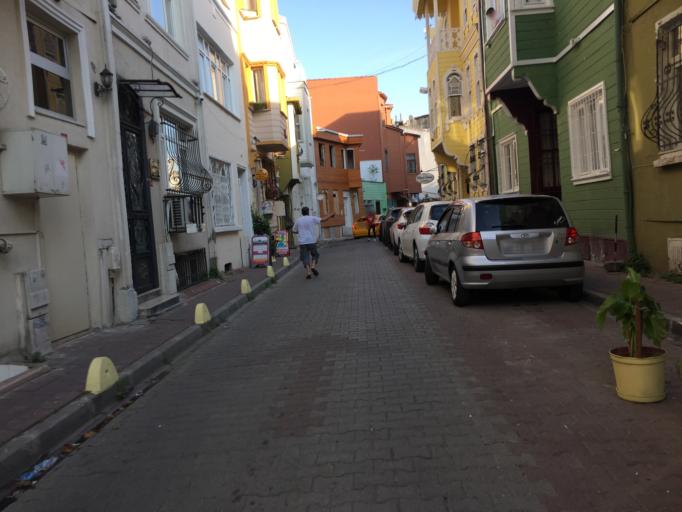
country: TR
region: Istanbul
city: Eminoenue
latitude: 41.0040
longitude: 28.9690
